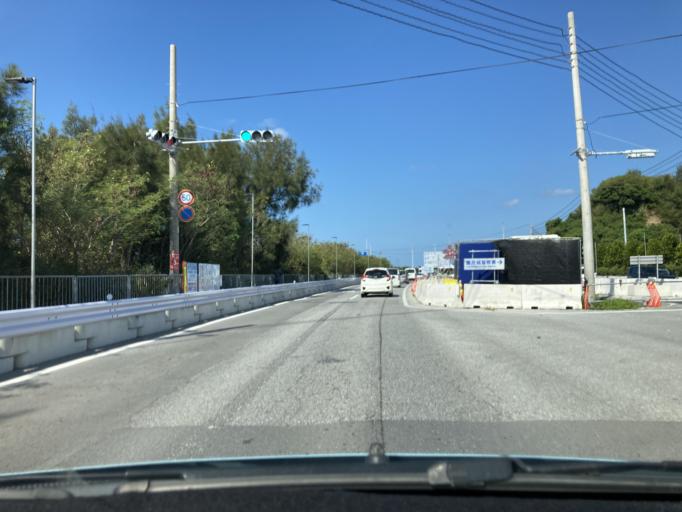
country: JP
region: Okinawa
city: Tomigusuku
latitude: 26.1743
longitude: 127.6548
